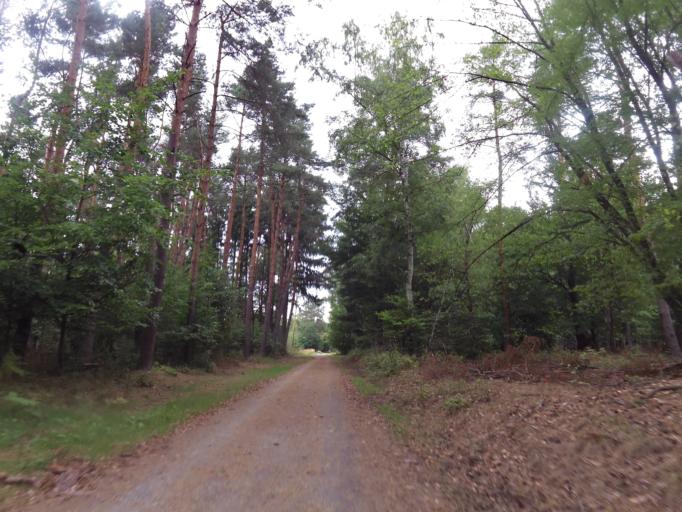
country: DE
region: Hesse
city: Morfelden-Walldorf
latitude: 50.0128
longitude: 8.5574
